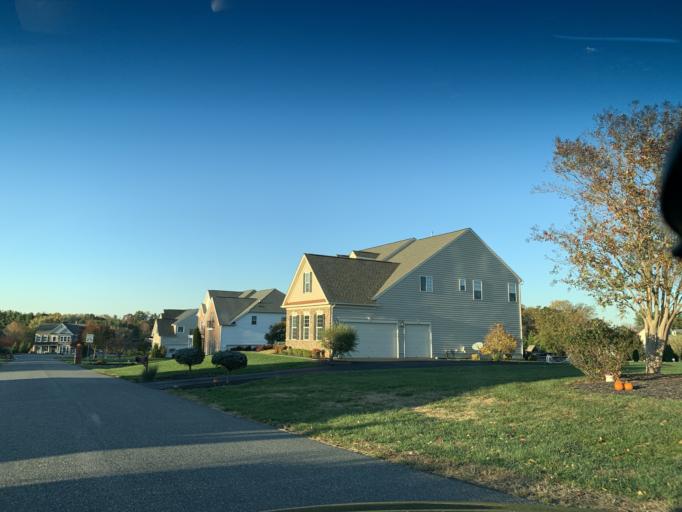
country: US
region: Maryland
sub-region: Harford County
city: Bel Air North
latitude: 39.5541
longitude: -76.4012
